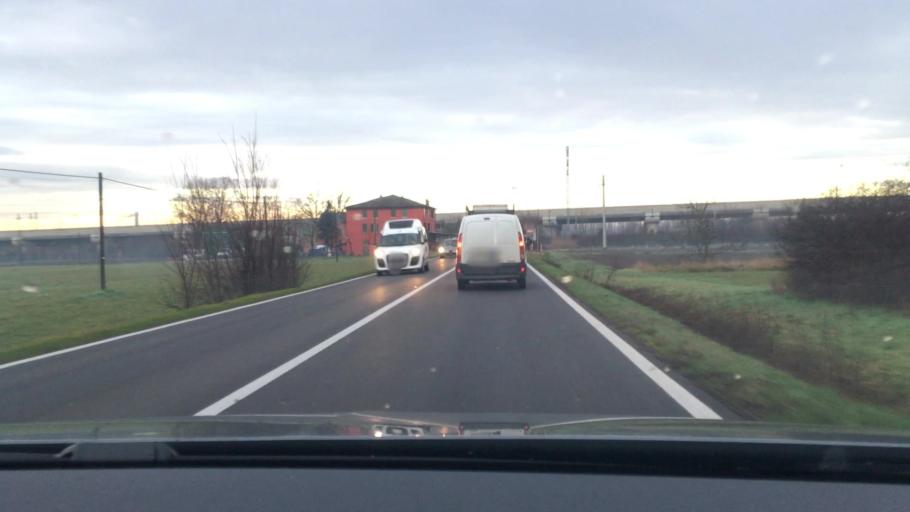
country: IT
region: Emilia-Romagna
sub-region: Provincia di Modena
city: Albareto
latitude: 44.6937
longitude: 10.9452
